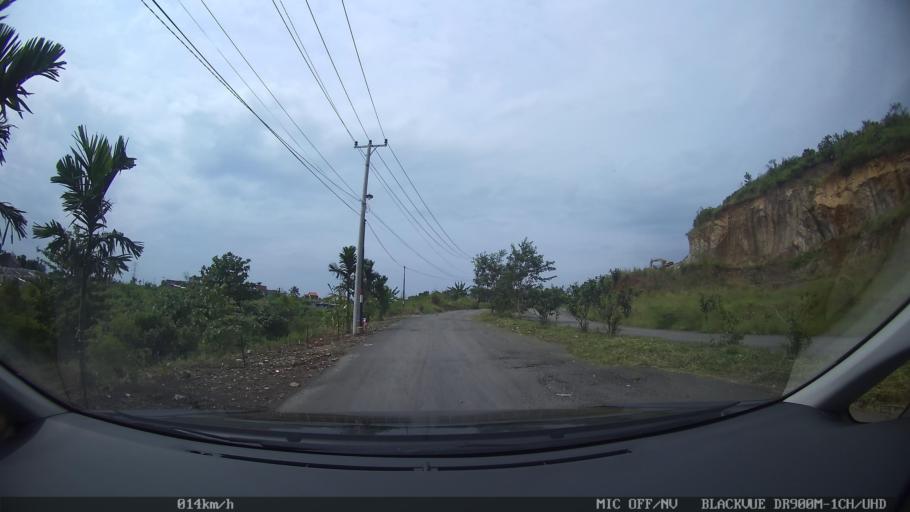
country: ID
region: Lampung
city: Bandarlampung
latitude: -5.4117
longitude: 105.1975
